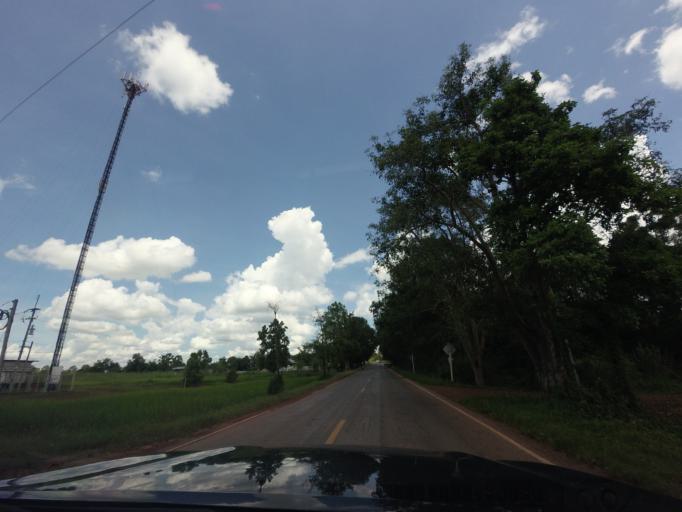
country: TH
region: Changwat Udon Thani
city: Ban Dung
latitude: 17.6589
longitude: 103.1485
